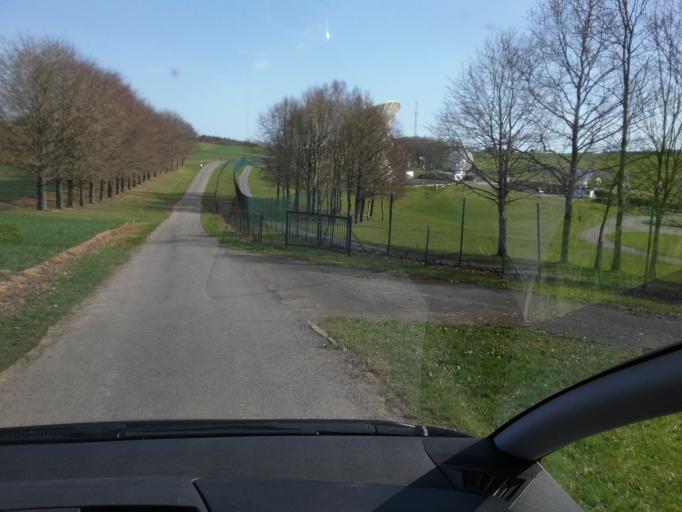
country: BE
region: Wallonia
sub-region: Province du Luxembourg
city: Daverdisse
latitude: 50.0040
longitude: 5.1467
